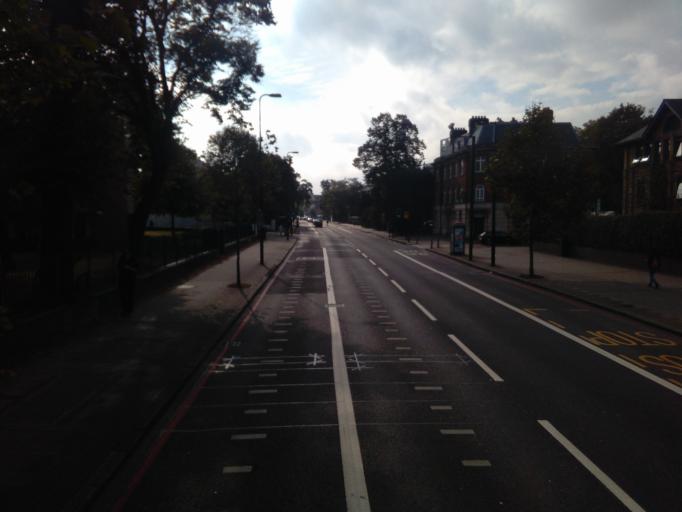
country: GB
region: England
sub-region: Greater London
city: Brixton
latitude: 51.4746
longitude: -0.1126
